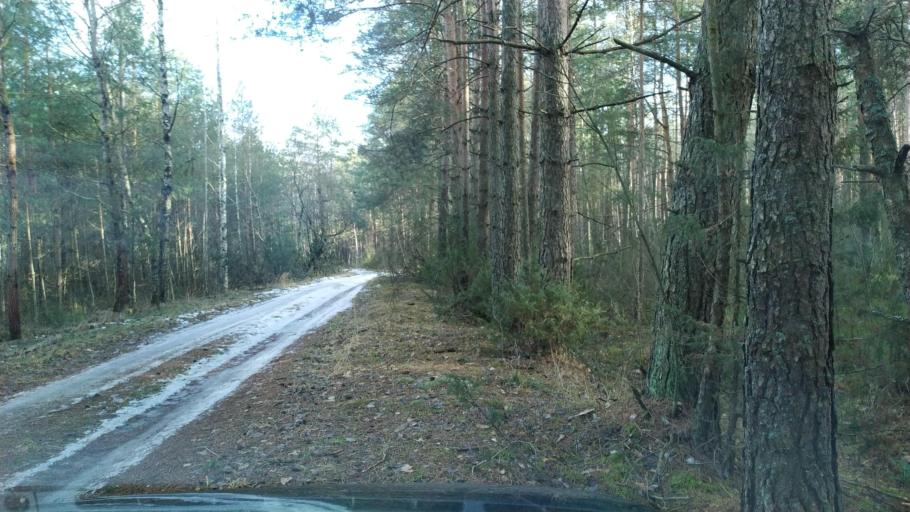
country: BY
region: Brest
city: Kamyanyets
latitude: 52.4313
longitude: 24.0051
